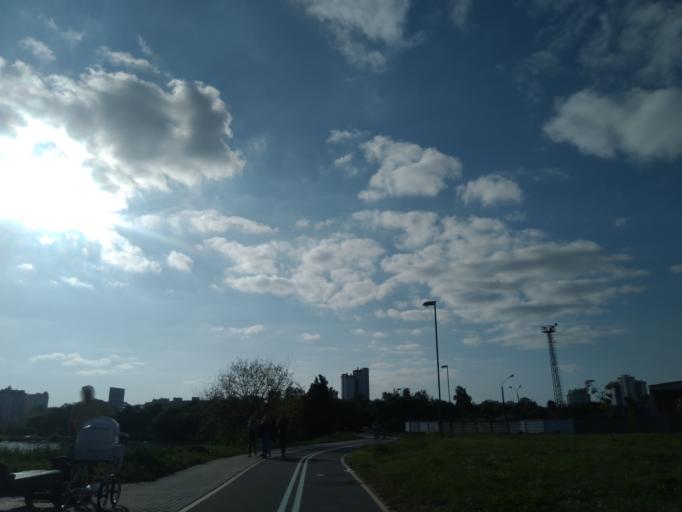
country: BY
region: Minsk
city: Minsk
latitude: 53.8766
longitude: 27.5813
